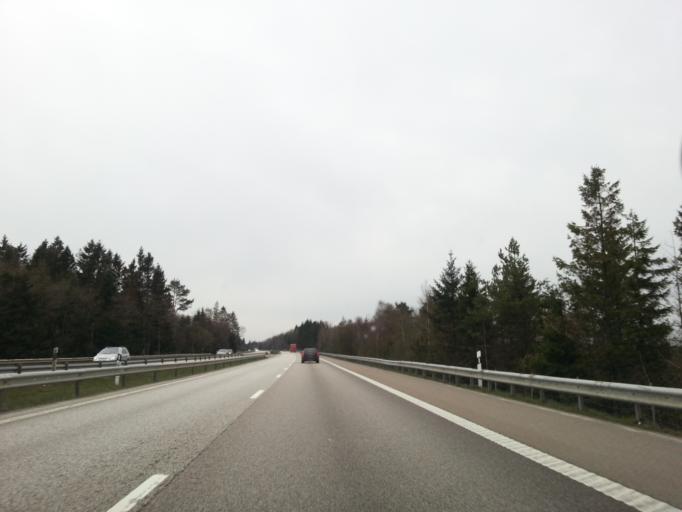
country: SE
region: Skane
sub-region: Bastads Kommun
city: Bastad
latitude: 56.3790
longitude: 12.9347
